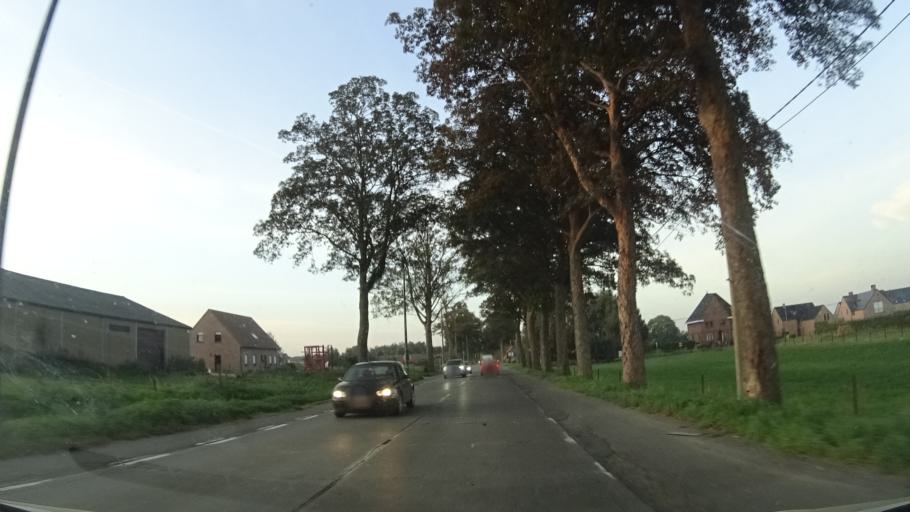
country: BE
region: Wallonia
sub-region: Province du Hainaut
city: Peruwelz
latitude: 50.5438
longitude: 3.6037
